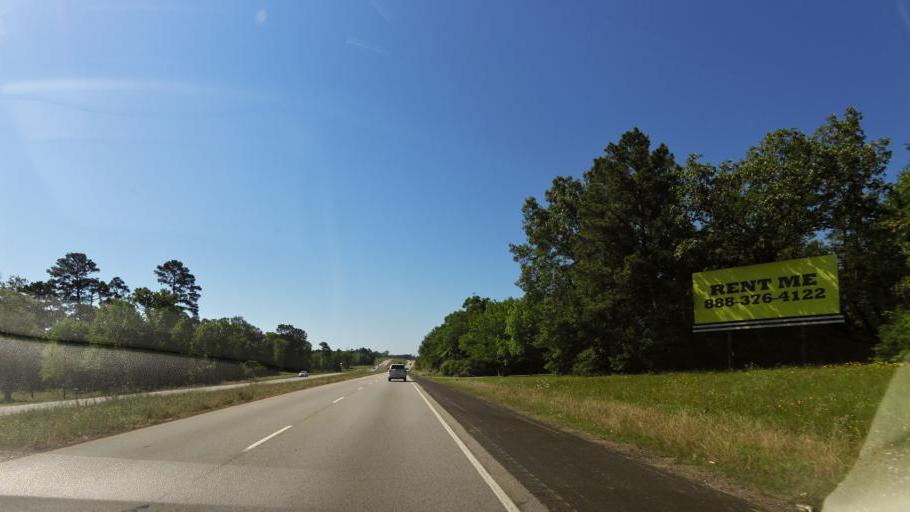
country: US
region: Texas
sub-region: Angelina County
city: Redland
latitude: 31.4246
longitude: -94.7250
